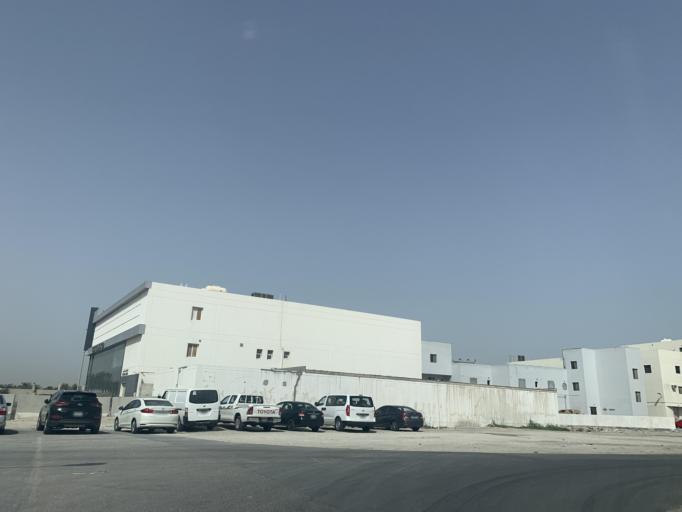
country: BH
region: Northern
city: Sitrah
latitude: 26.1588
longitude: 50.6073
